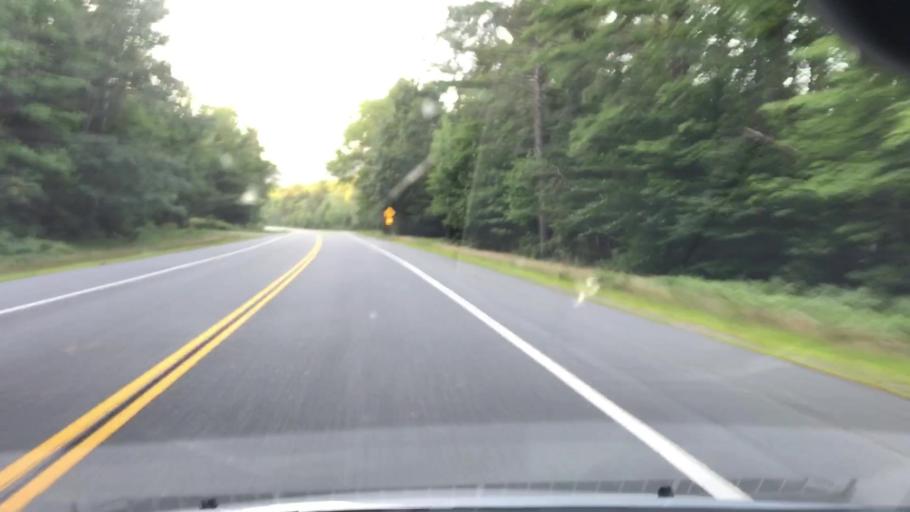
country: US
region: New Hampshire
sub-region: Grafton County
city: Rumney
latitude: 43.9596
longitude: -71.8870
